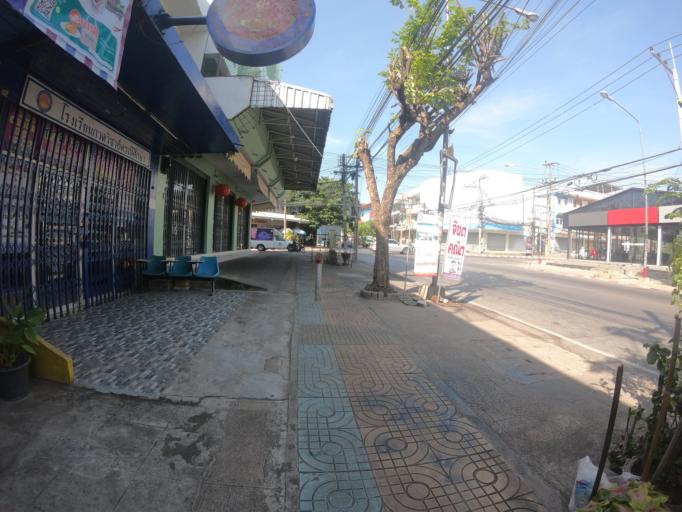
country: TH
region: Khon Kaen
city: Khon Kaen
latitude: 16.4364
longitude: 102.8345
